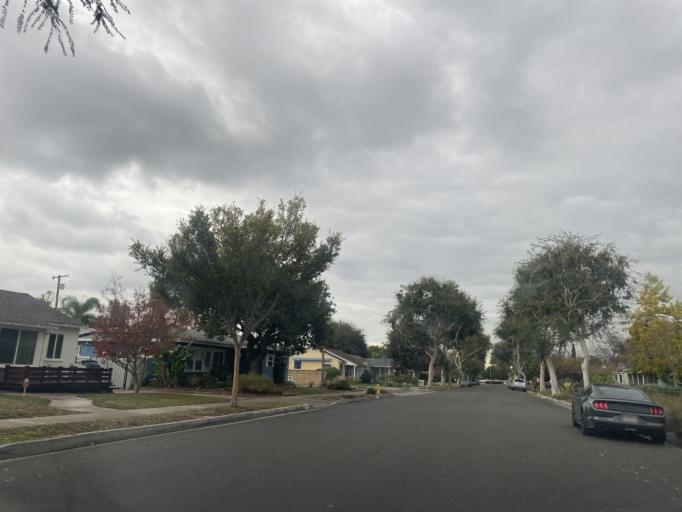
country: US
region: California
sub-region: Orange County
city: Fullerton
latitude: 33.8766
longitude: -117.9043
